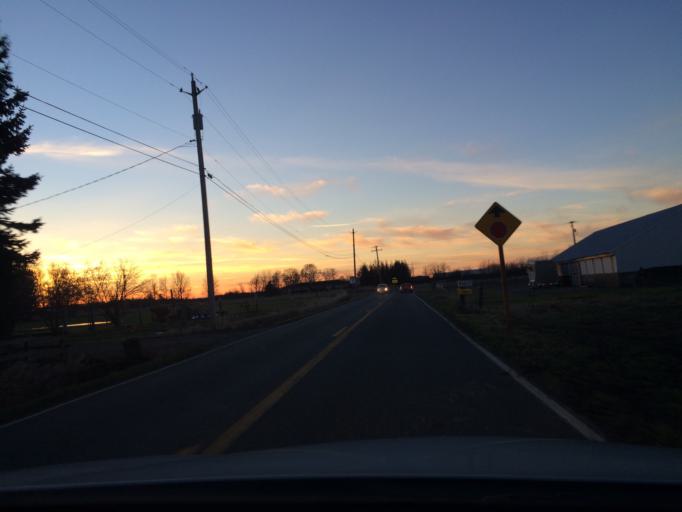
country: US
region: Washington
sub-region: Whatcom County
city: Everson
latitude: 48.9346
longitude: -122.3404
